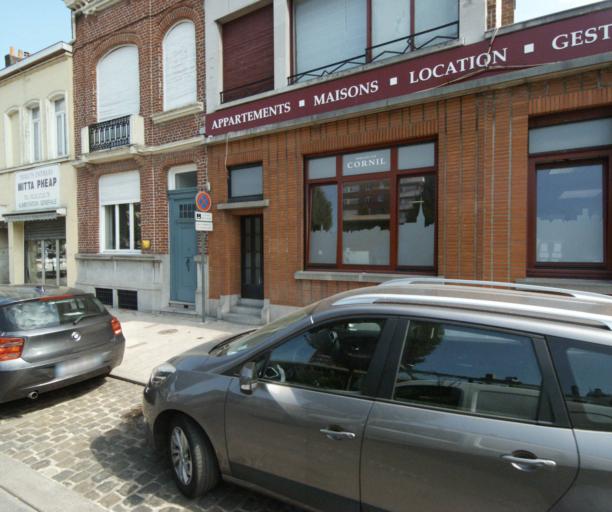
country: FR
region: Nord-Pas-de-Calais
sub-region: Departement du Nord
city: Tourcoing
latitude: 50.7216
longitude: 3.1579
